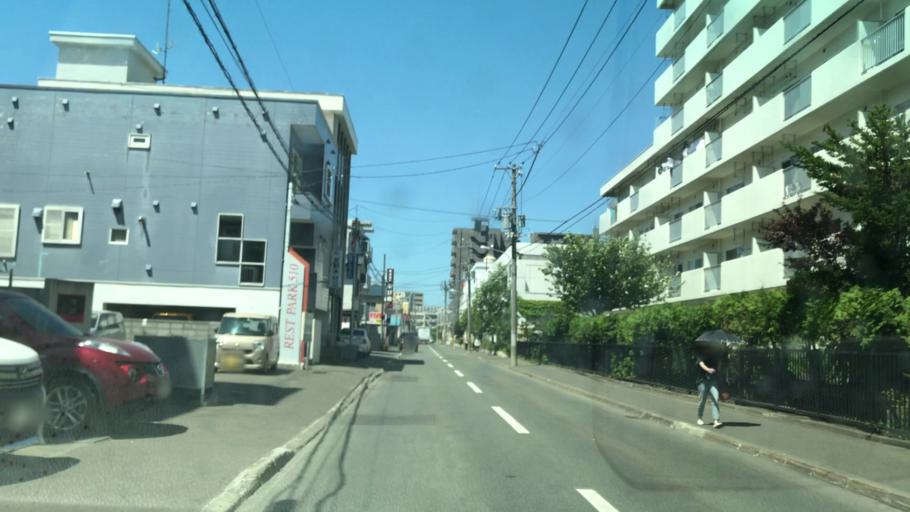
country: JP
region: Hokkaido
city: Sapporo
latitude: 43.0459
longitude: 141.3764
